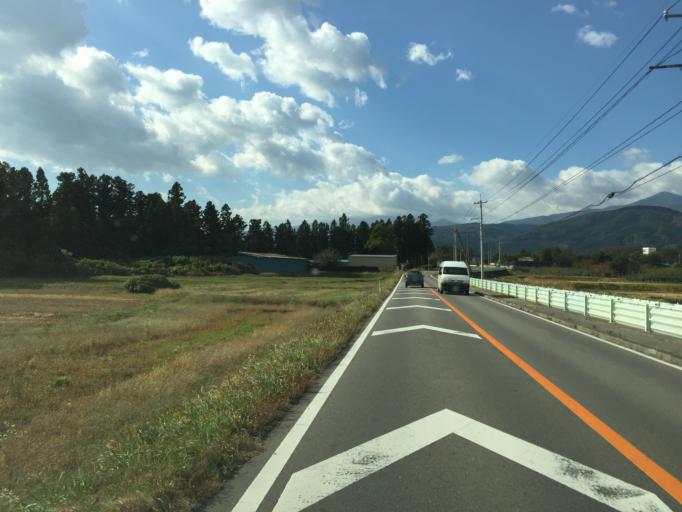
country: JP
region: Fukushima
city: Fukushima-shi
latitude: 37.7633
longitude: 140.3791
